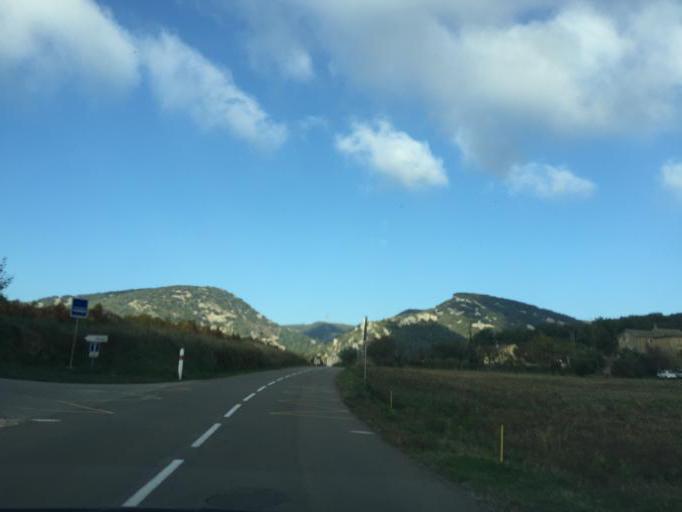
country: FR
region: Rhone-Alpes
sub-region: Departement de l'Ardeche
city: Bourg-Saint-Andeol
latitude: 44.4382
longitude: 4.6298
